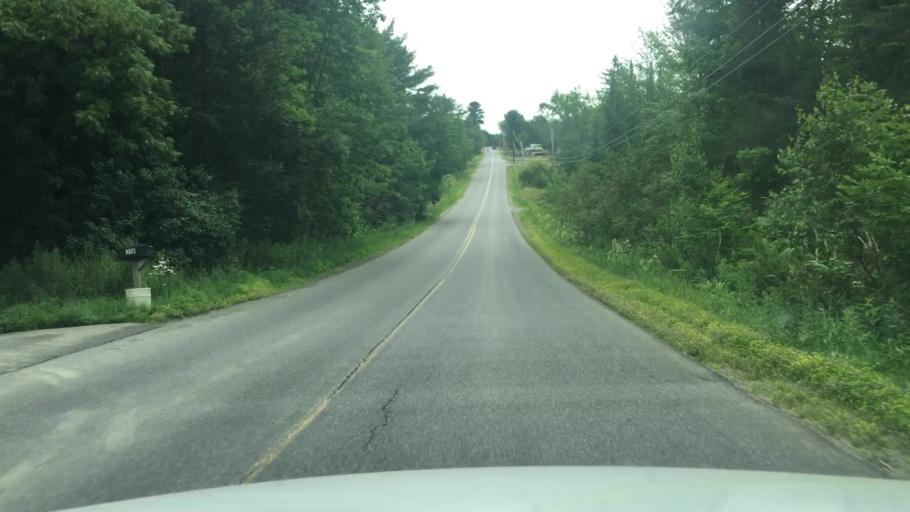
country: US
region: Maine
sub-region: Kennebec County
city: Clinton
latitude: 44.5821
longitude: -69.4923
